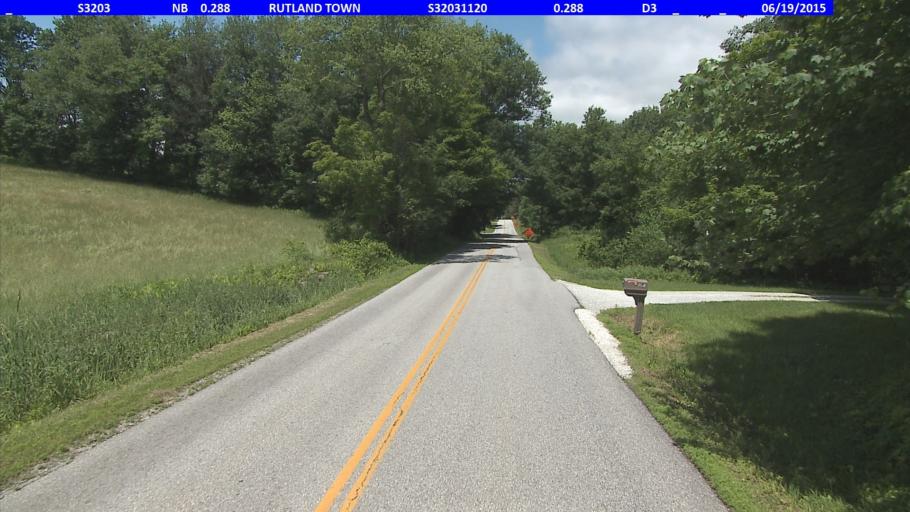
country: US
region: Vermont
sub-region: Rutland County
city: Rutland
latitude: 43.6576
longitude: -72.9975
